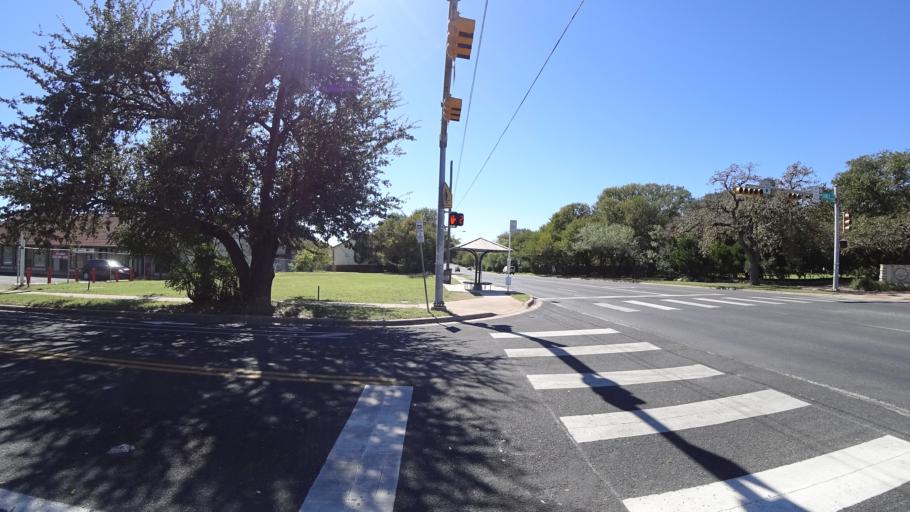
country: US
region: Texas
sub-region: Travis County
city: Rollingwood
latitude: 30.2256
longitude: -97.8037
